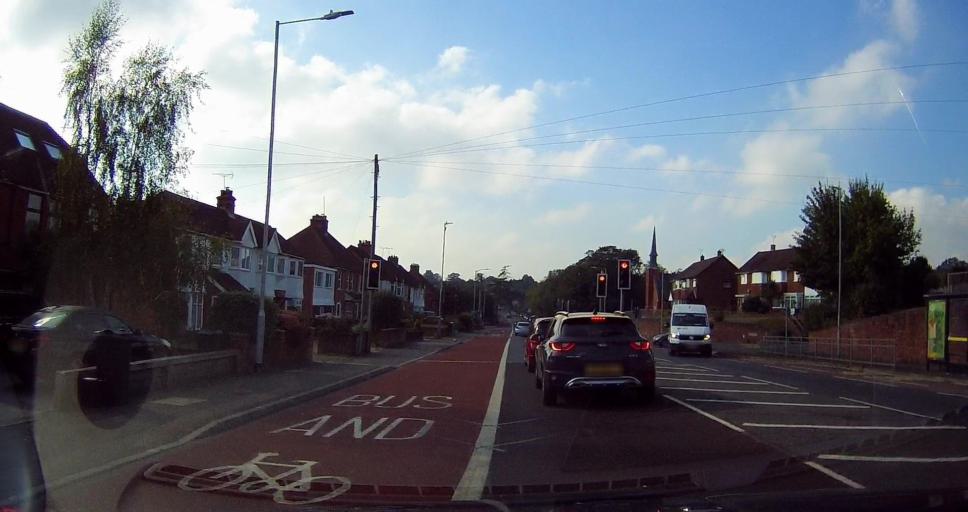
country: GB
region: England
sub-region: Kent
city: Kennington
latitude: 51.1587
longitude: 0.8830
